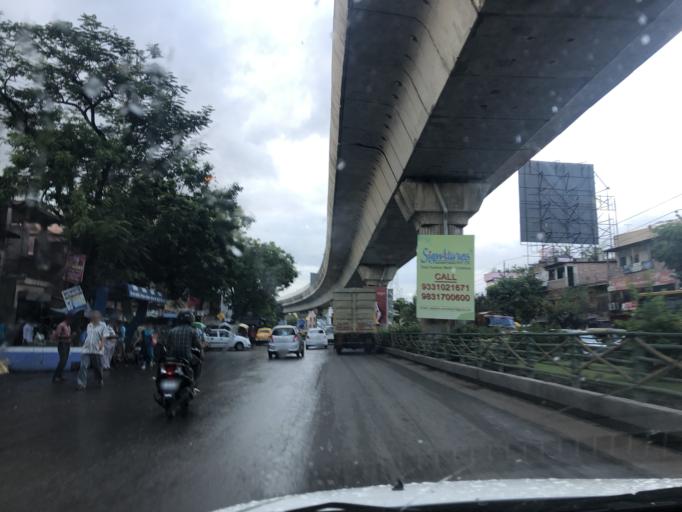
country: IN
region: West Bengal
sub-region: South 24 Paraganas
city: Santoshpur
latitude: 22.4685
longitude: 88.3091
